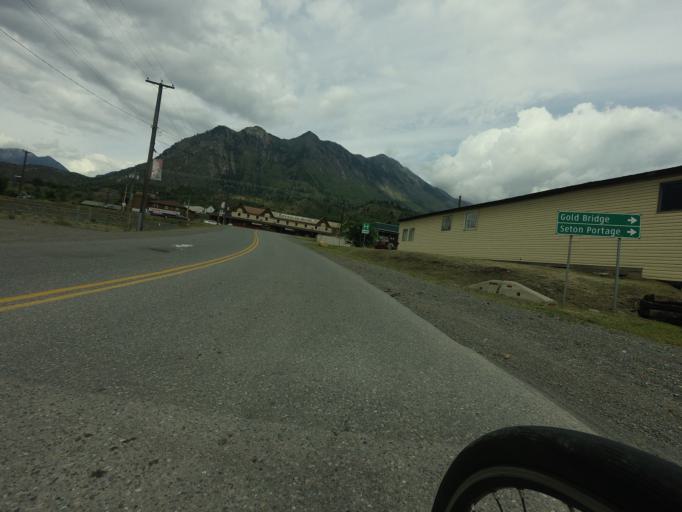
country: CA
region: British Columbia
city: Lillooet
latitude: 50.6863
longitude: -121.9355
